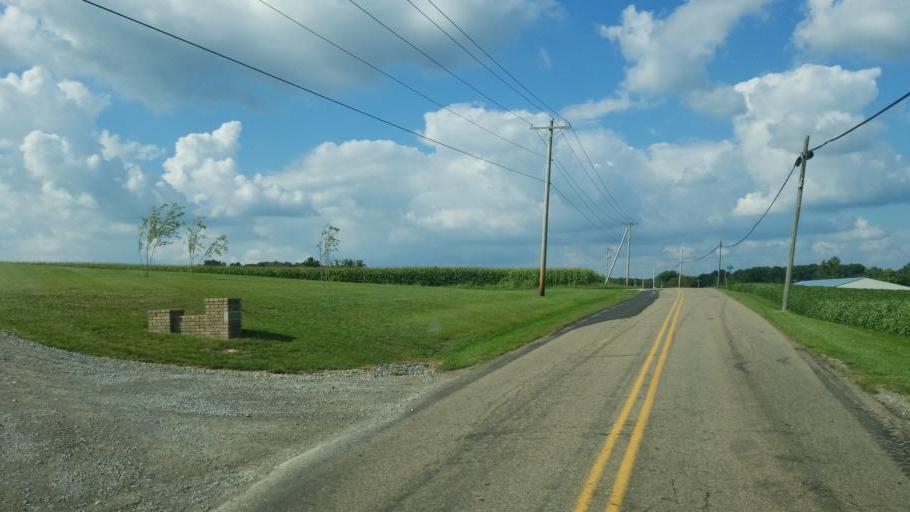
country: US
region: Ohio
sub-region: Knox County
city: Danville
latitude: 40.4408
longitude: -82.3035
